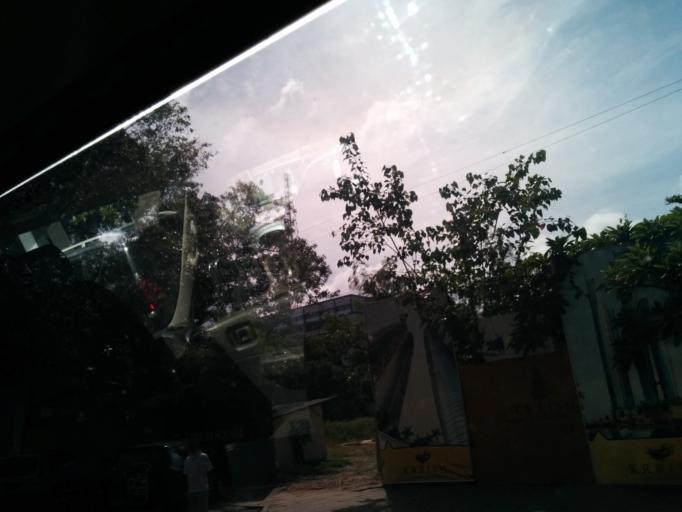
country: LK
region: Western
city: Colombo
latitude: 6.9334
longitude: 79.8449
